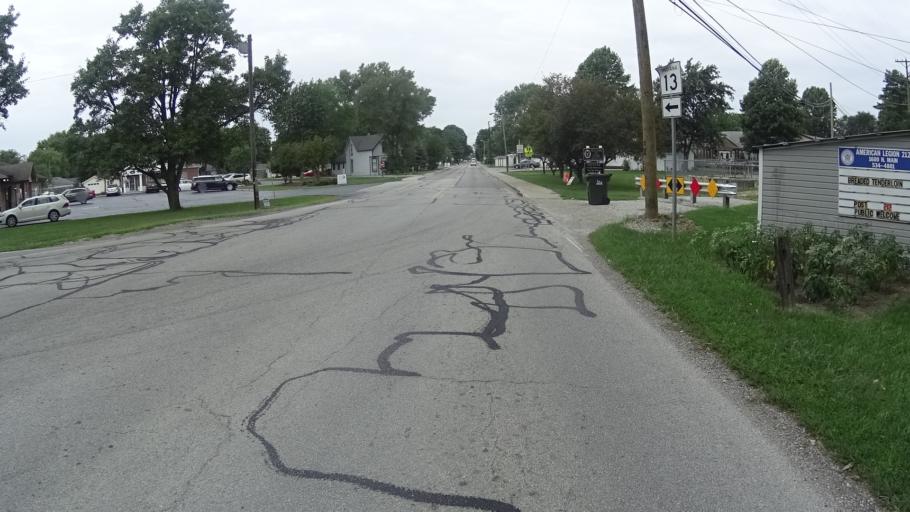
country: US
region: Indiana
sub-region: Madison County
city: Lapel
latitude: 40.0636
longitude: -85.8438
